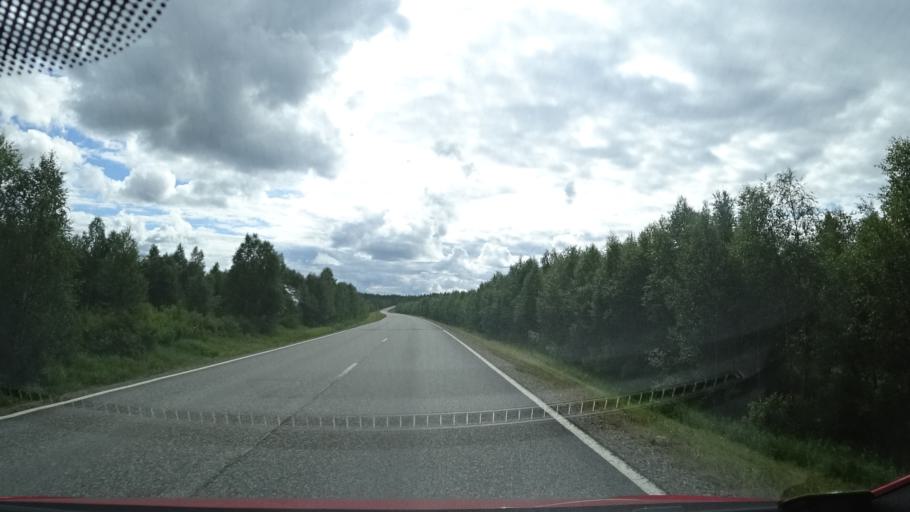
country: FI
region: Lapland
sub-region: Tunturi-Lappi
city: Kittilae
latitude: 67.5653
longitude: 24.9200
